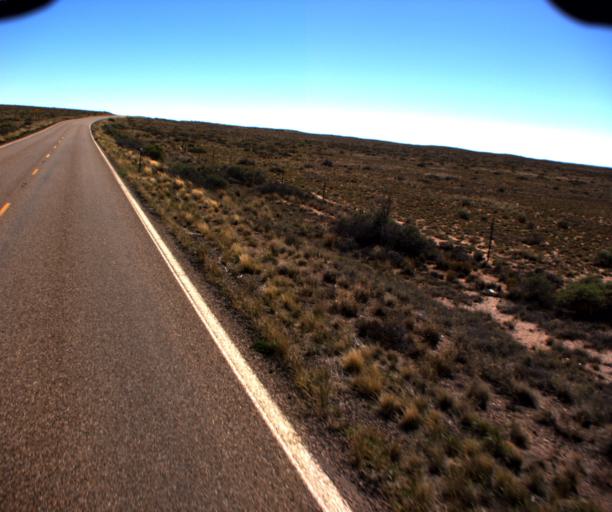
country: US
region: Arizona
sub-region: Navajo County
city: Holbrook
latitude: 35.0397
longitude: -110.0918
